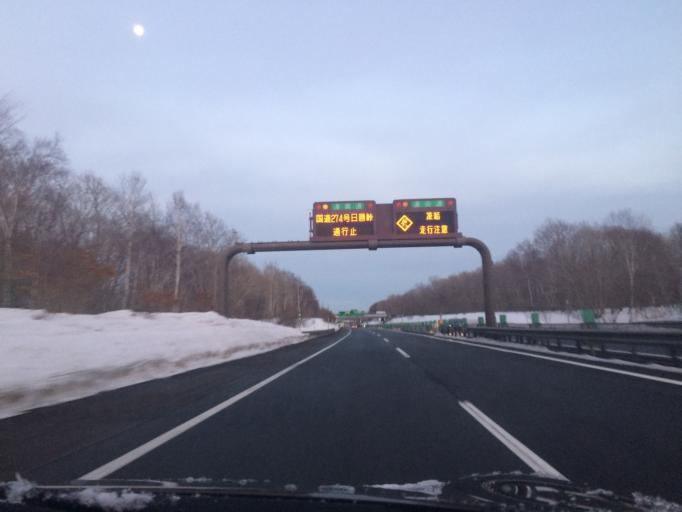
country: JP
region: Hokkaido
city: Chitose
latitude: 42.8494
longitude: 141.5736
